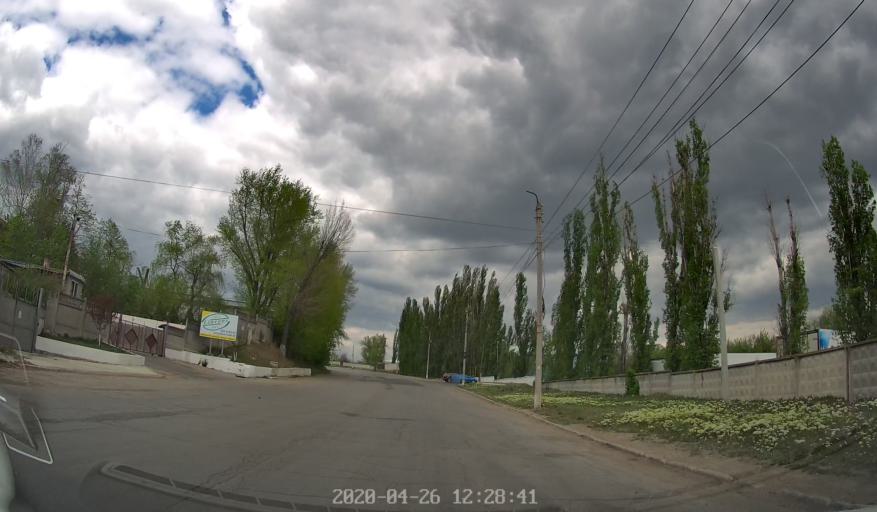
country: MD
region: Chisinau
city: Chisinau
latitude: 46.9981
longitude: 28.9068
